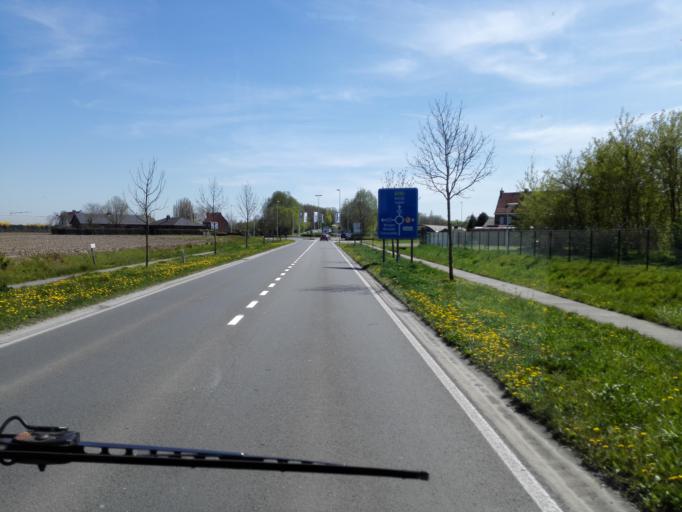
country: BE
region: Flanders
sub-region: Provincie West-Vlaanderen
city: Ingelmunster
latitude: 50.9201
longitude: 3.2664
